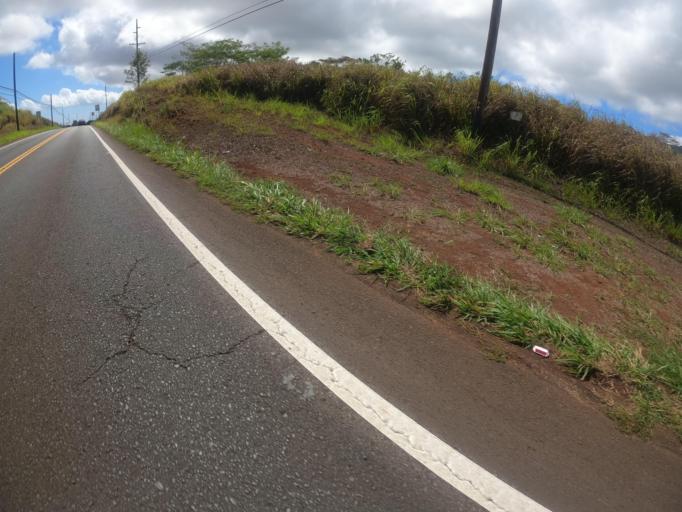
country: US
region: Hawaii
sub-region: Honolulu County
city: Schofield Barracks
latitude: 21.4505
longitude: -158.0602
